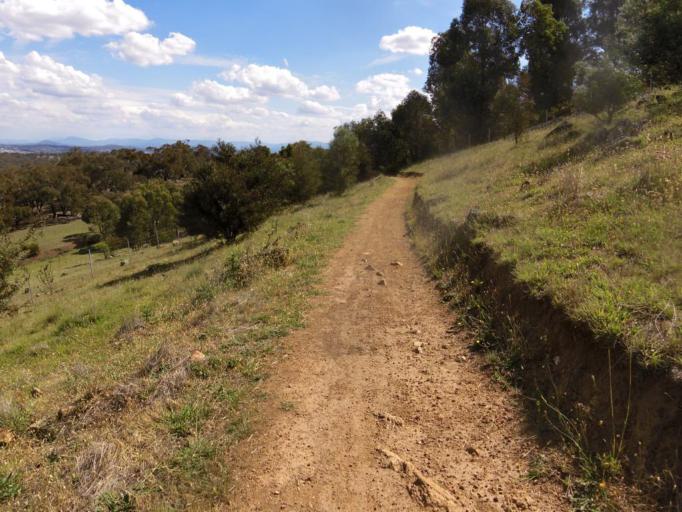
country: AU
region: Australian Capital Territory
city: Belconnen
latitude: -35.1525
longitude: 149.0866
